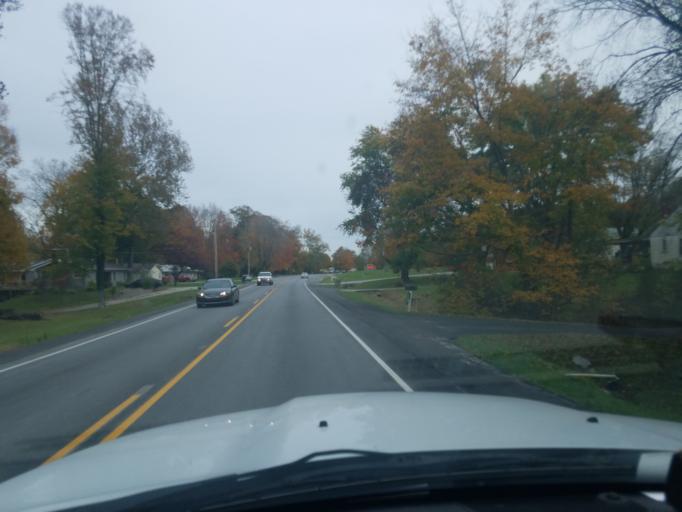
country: US
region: Indiana
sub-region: Washington County
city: New Pekin
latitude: 38.4569
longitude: -85.9253
